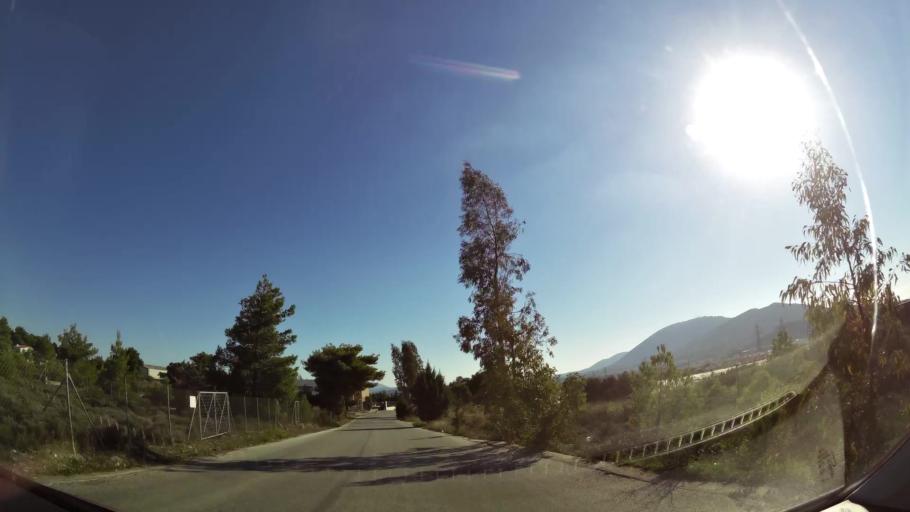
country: GR
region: Attica
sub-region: Nomarchia Anatolikis Attikis
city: Anthousa
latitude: 38.0236
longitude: 23.8675
